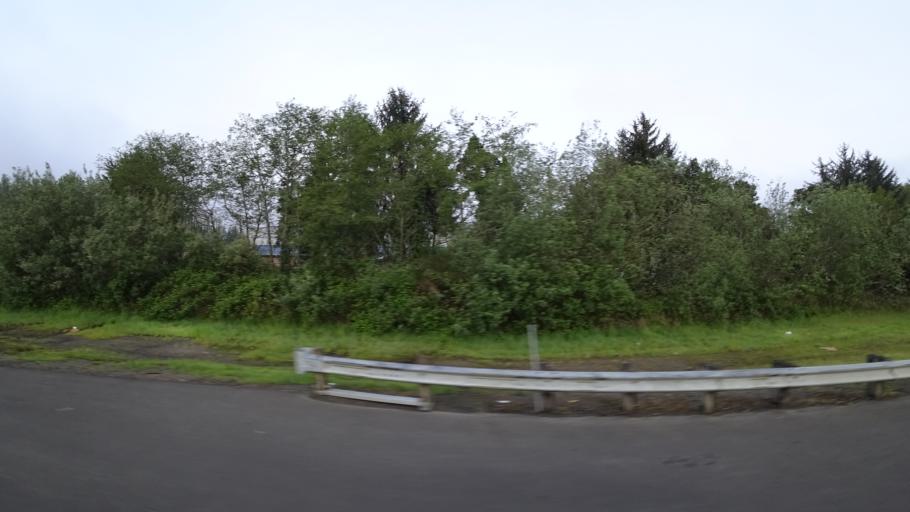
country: US
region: Oregon
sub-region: Douglas County
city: Reedsport
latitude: 43.7165
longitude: -124.0992
